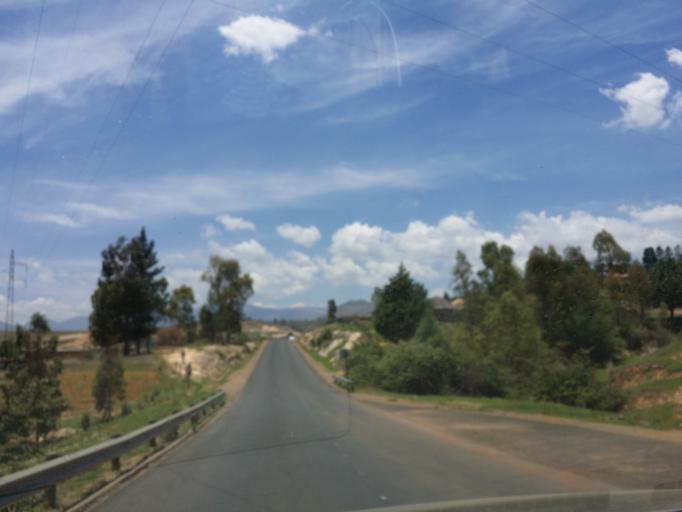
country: LS
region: Butha-Buthe
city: Butha-Buthe
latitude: -28.7348
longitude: 28.4299
